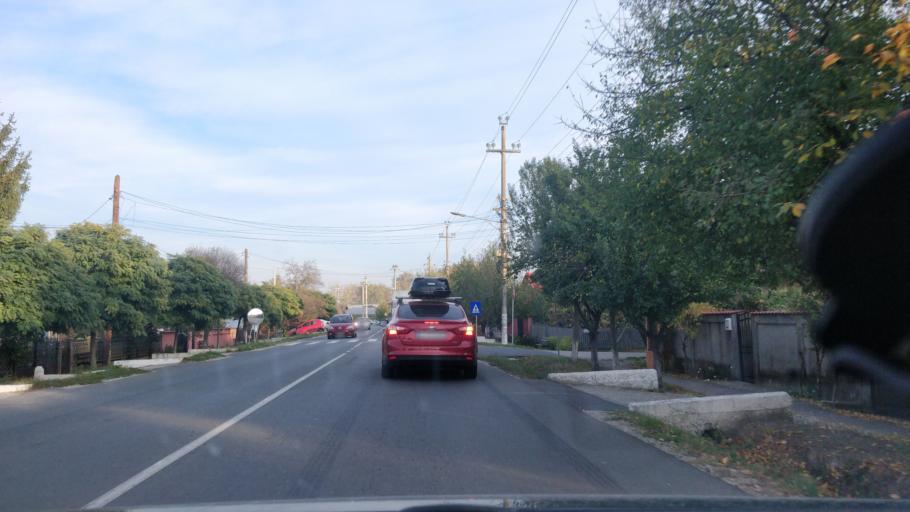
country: RO
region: Ilfov
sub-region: Comuna Ciorogarla
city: Ciorogarla
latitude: 44.4432
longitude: 25.8730
